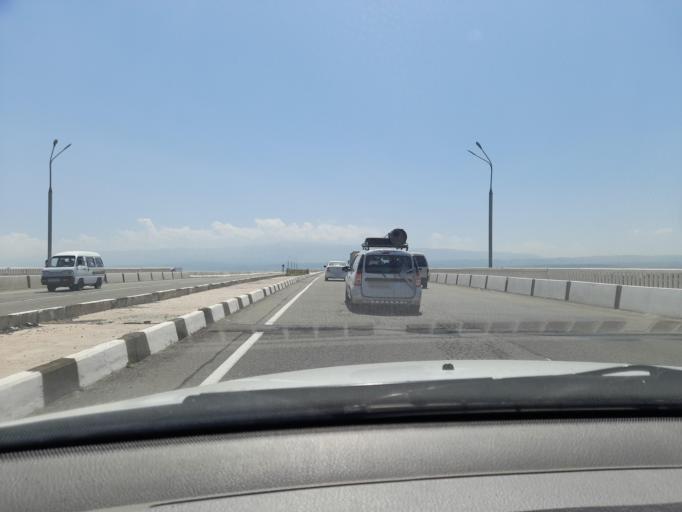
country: UZ
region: Jizzax
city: Jizzax
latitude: 40.0960
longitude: 67.9391
